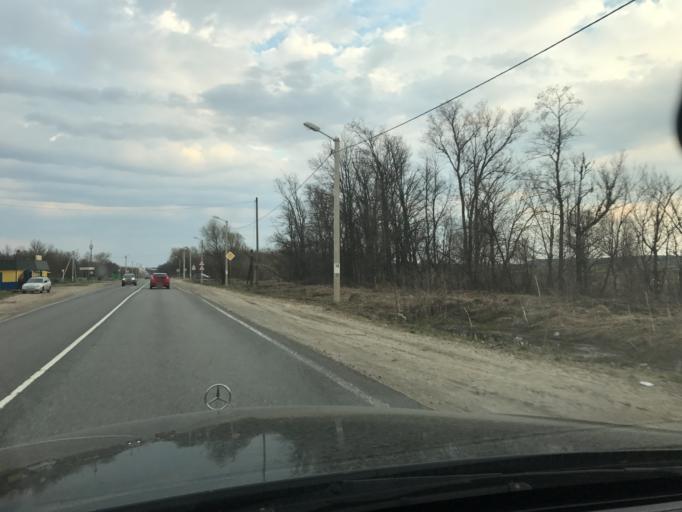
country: RU
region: Vladimir
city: Krasnaya Gorbatka
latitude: 55.6580
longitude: 41.8136
